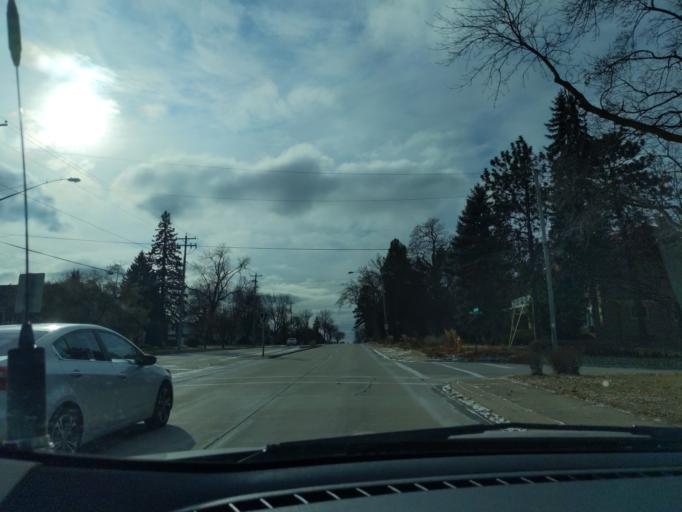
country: US
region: Wisconsin
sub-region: Brown County
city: Allouez
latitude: 44.4758
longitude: -88.0278
